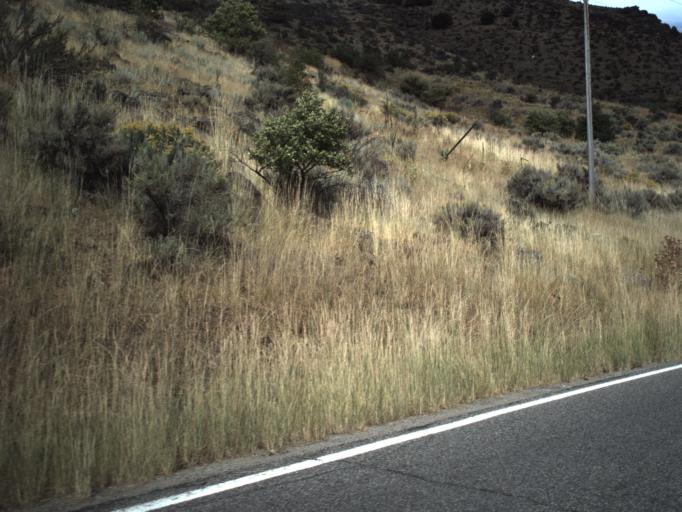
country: US
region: Utah
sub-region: Cache County
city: Millville
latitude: 41.6119
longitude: -111.6307
